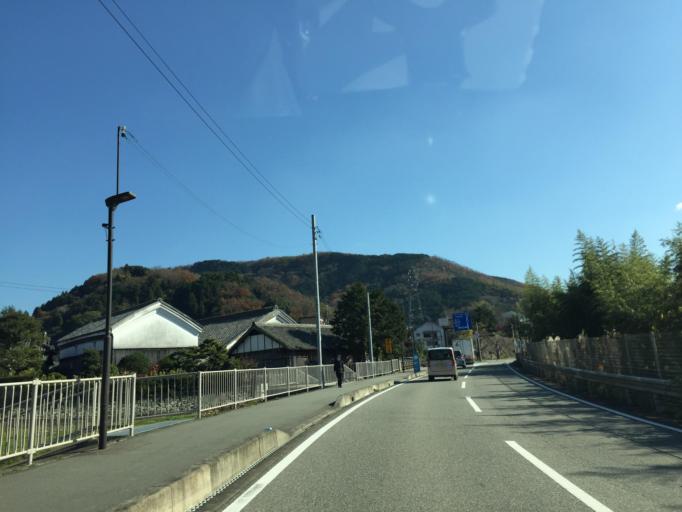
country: JP
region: Wakayama
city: Iwade
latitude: 34.1659
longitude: 135.3038
